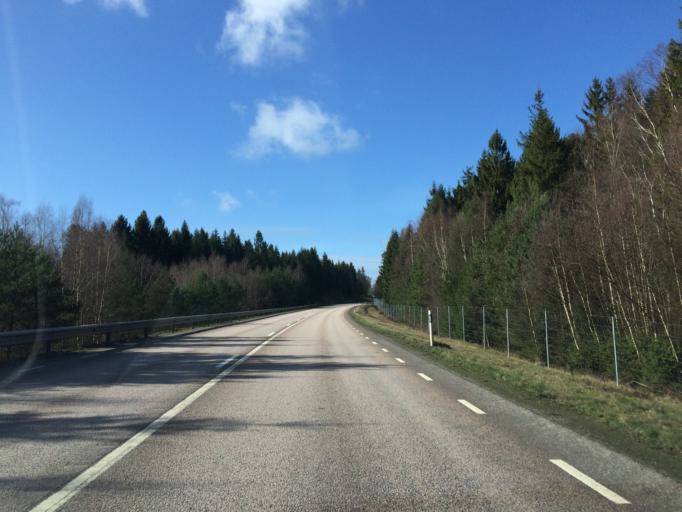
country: SE
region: Halland
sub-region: Laholms Kommun
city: Knared
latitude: 56.5225
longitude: 13.2566
